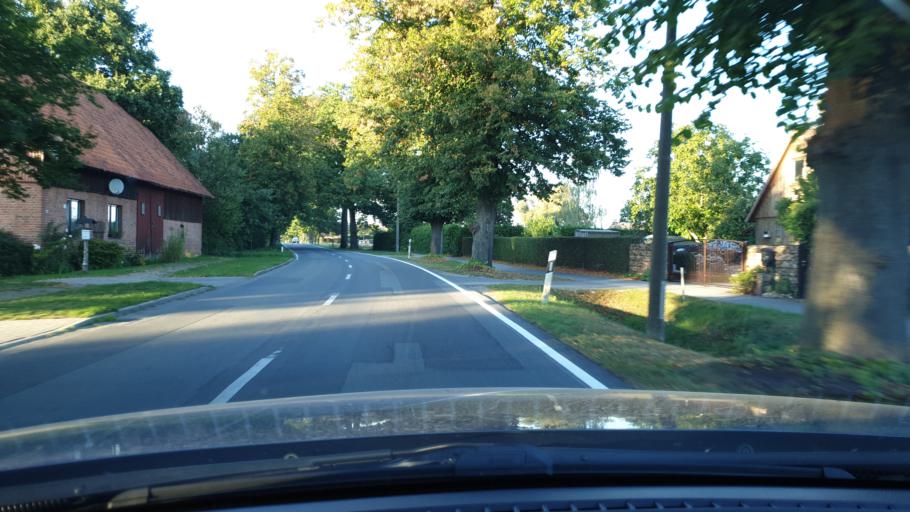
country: DE
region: Mecklenburg-Vorpommern
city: Wittenburg
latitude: 53.5414
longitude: 11.0860
